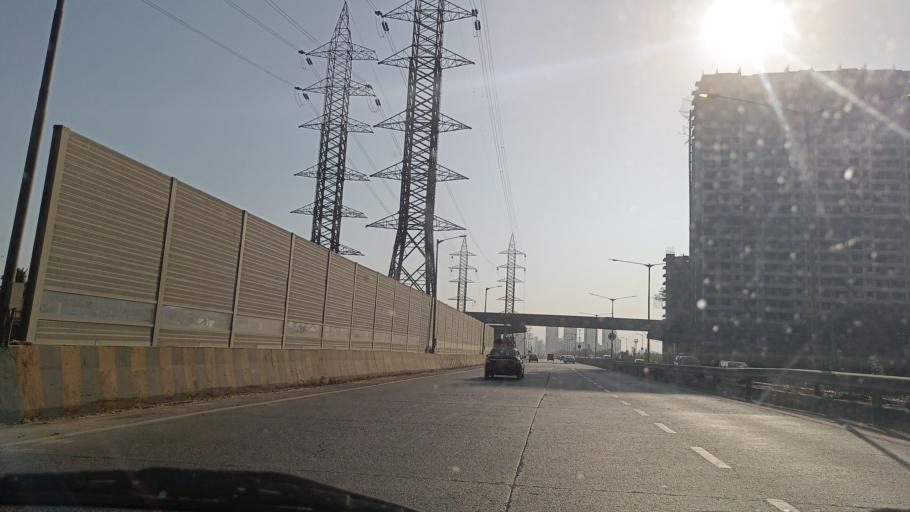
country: IN
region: Maharashtra
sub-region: Mumbai Suburban
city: Mumbai
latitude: 19.0333
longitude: 72.8976
